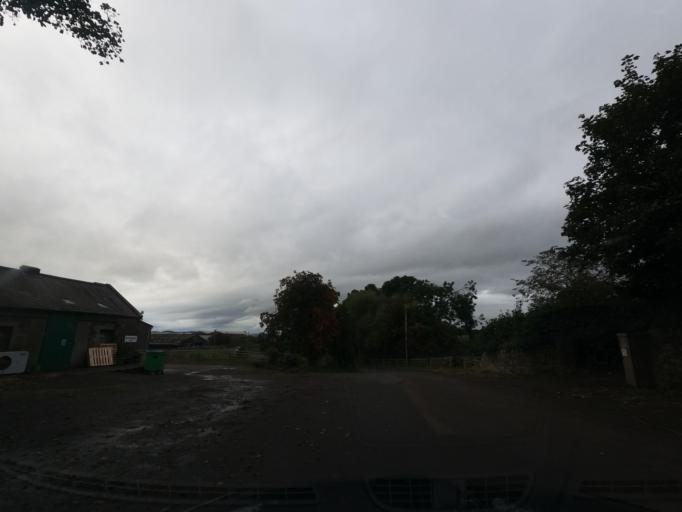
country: GB
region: England
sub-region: Northumberland
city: Doddington
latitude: 55.5870
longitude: -2.0056
